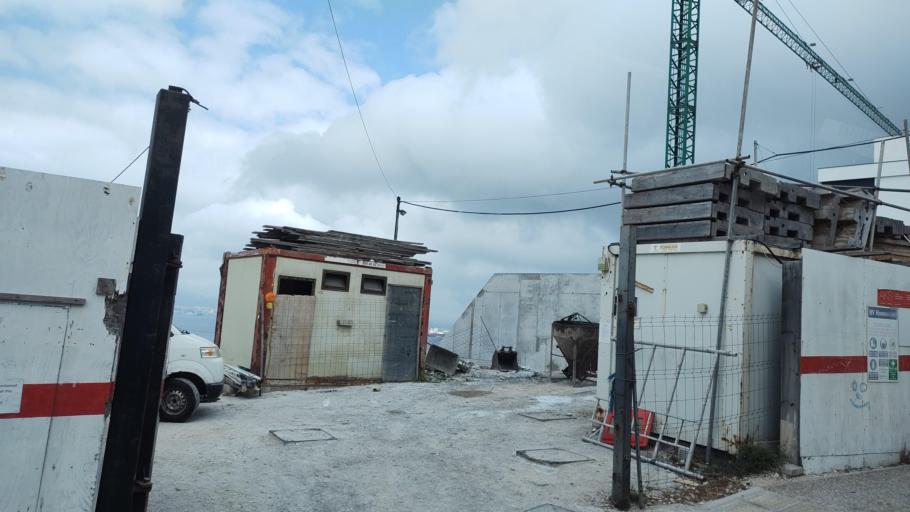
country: GI
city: Gibraltar
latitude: 36.1162
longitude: -5.3484
